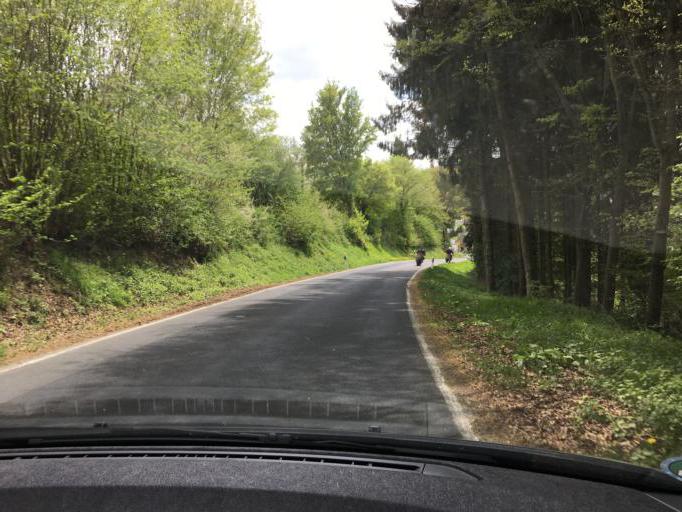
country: DE
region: Rheinland-Pfalz
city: Kirchsahr
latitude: 50.5019
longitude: 6.9066
